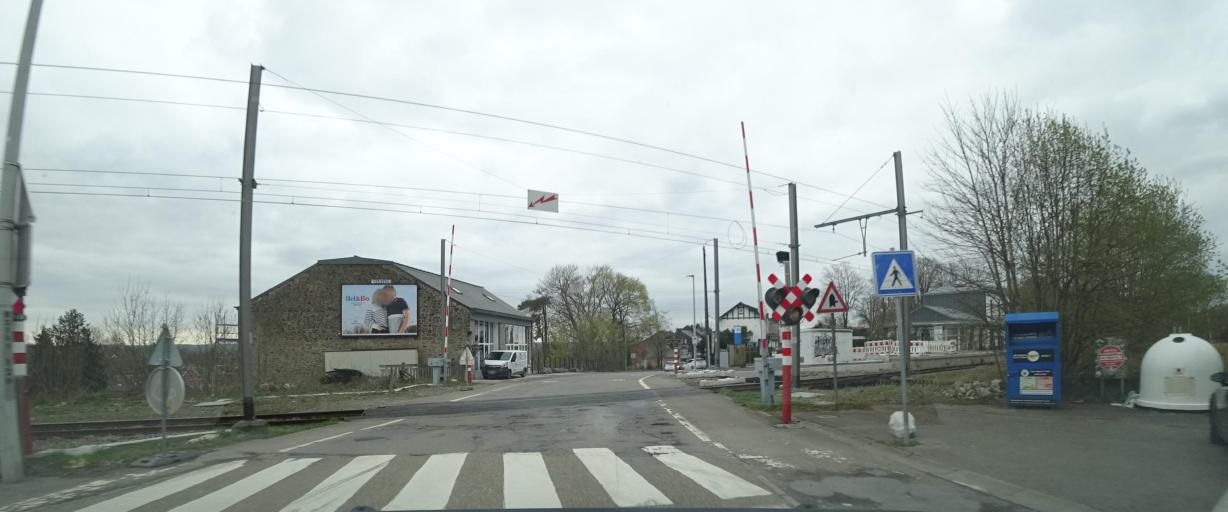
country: BE
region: Wallonia
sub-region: Province du Luxembourg
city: Marche-en-Famenne
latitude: 50.2219
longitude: 5.3453
